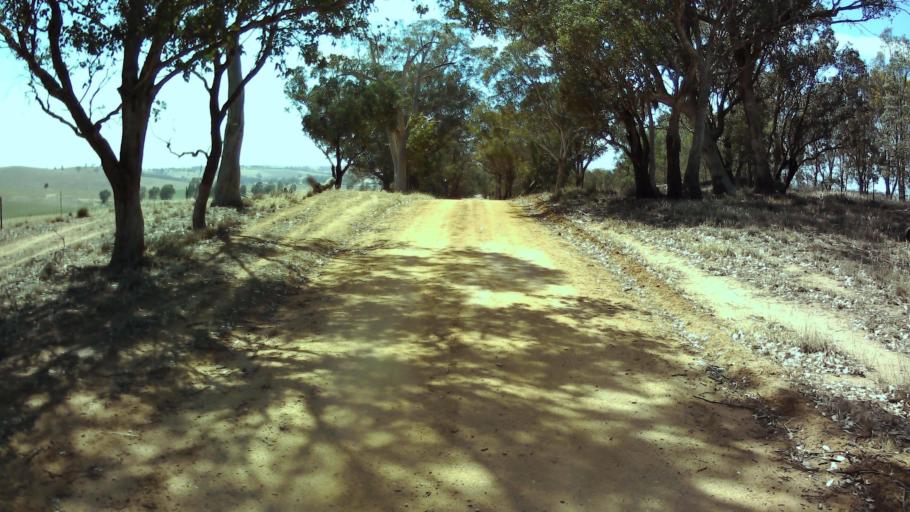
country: AU
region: New South Wales
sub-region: Weddin
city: Grenfell
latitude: -33.9545
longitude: 148.4111
